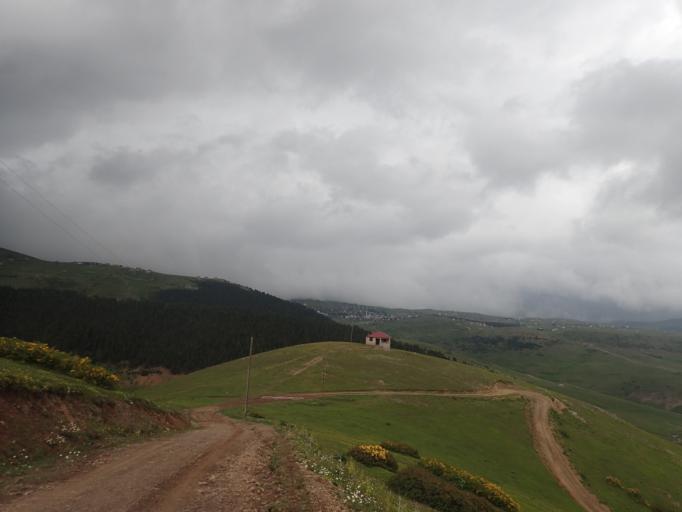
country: TR
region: Ordu
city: Yesilce
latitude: 40.6040
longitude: 37.9545
